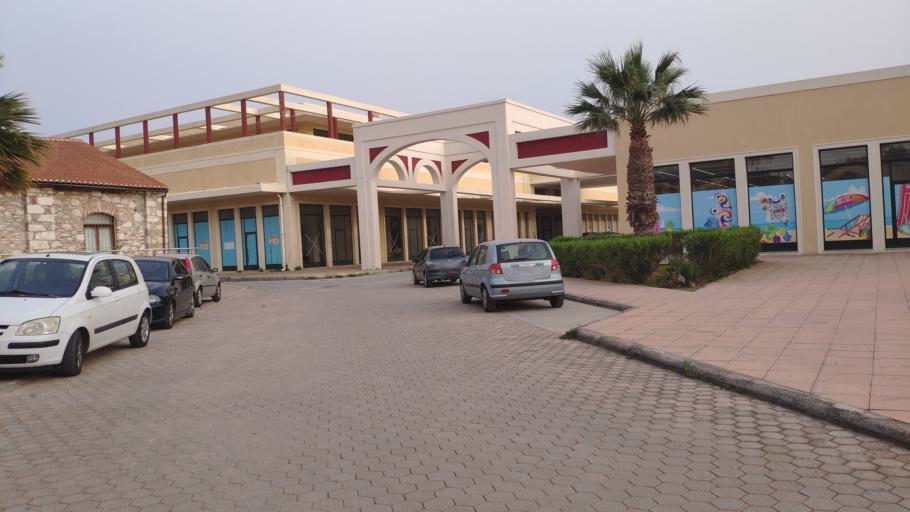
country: GR
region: Attica
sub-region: Nomarchia Anatolikis Attikis
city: Lavrio
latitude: 37.7117
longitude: 24.0541
